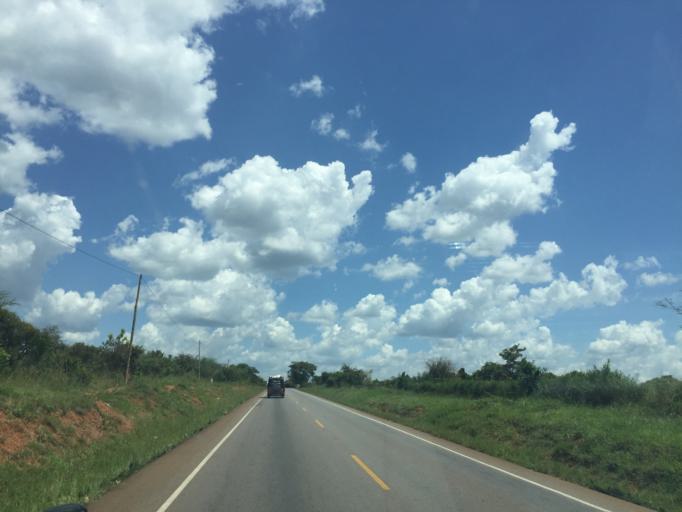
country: UG
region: Central Region
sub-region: Nakasongola District
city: Nakasongola
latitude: 1.3438
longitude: 32.3927
